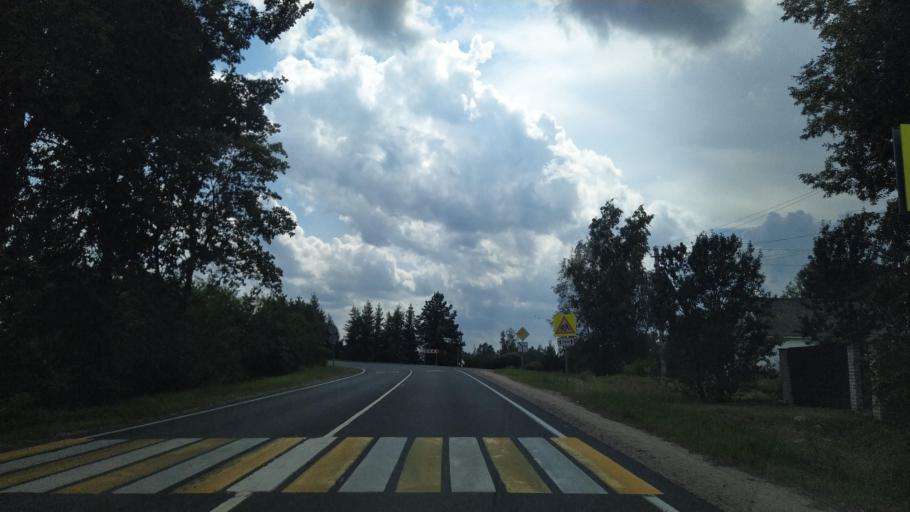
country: RU
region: Pskov
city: Pskov
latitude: 57.7565
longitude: 28.7717
